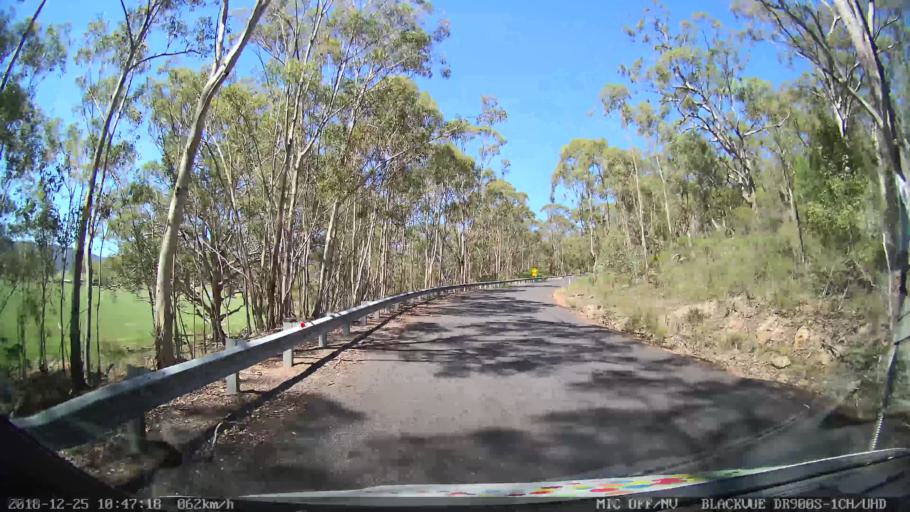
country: AU
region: New South Wales
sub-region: Upper Hunter Shire
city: Merriwa
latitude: -32.4471
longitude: 150.2774
